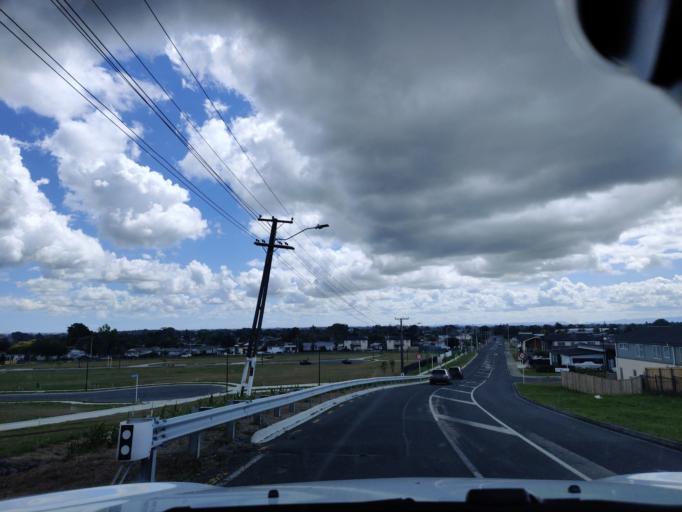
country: NZ
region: Auckland
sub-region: Auckland
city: Red Hill
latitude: -37.0532
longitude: 174.9688
